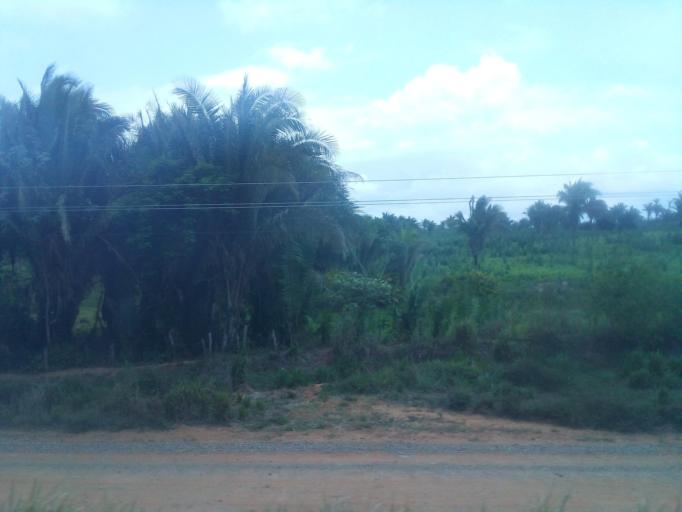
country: BR
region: Maranhao
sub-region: Santa Ines
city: Santa Ines
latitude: -3.7198
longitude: -45.5183
